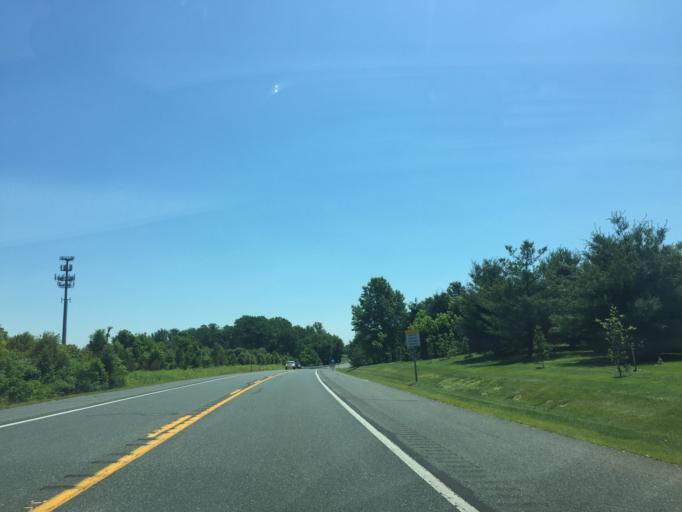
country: US
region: Maryland
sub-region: Harford County
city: Bel Air North
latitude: 39.5759
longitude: -76.3809
